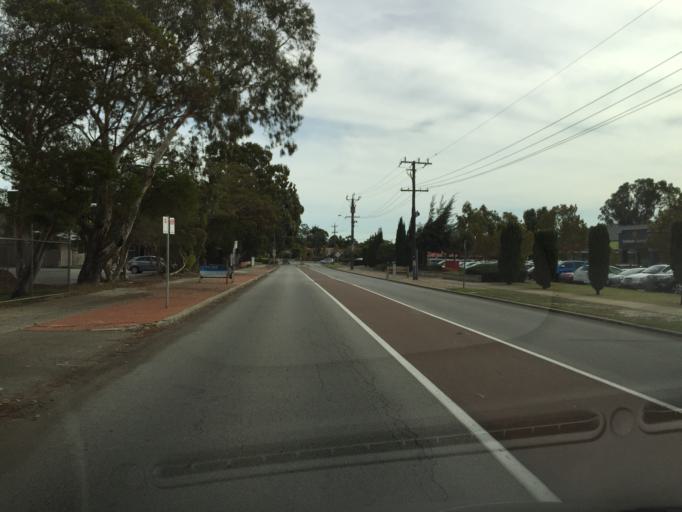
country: AU
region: Western Australia
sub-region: Canning
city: Willetton
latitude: -32.0590
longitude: 115.8804
